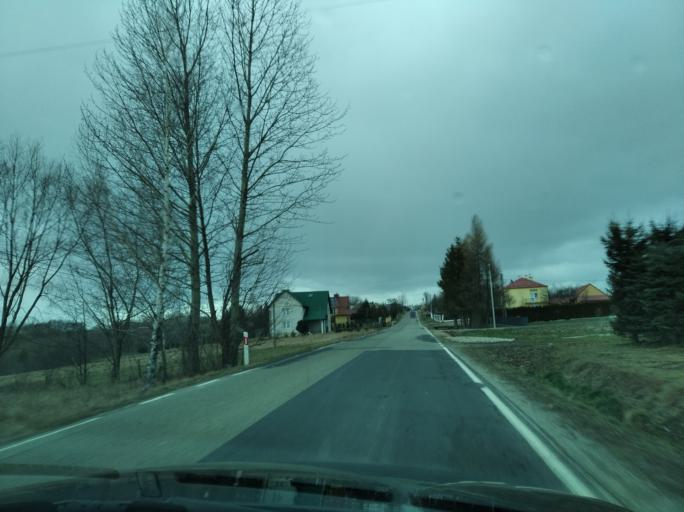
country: PL
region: Subcarpathian Voivodeship
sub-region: Powiat rzeszowski
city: Hyzne
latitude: 49.9264
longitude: 22.1924
